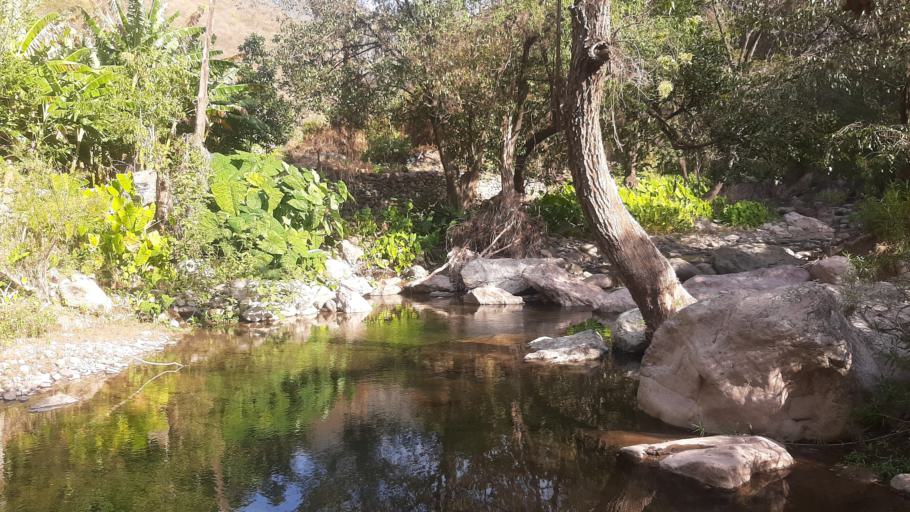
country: MX
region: Durango
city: Santa Catarina de Tepehuanes
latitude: 25.3703
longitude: -106.4323
